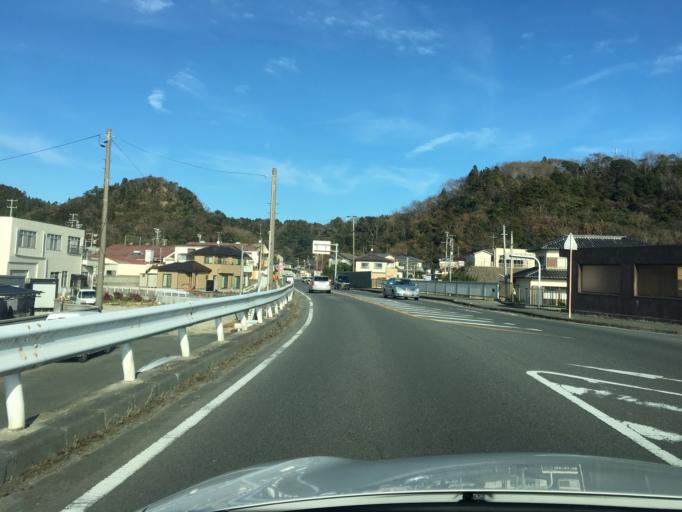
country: JP
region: Fukushima
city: Iwaki
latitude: 36.9558
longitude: 140.9404
